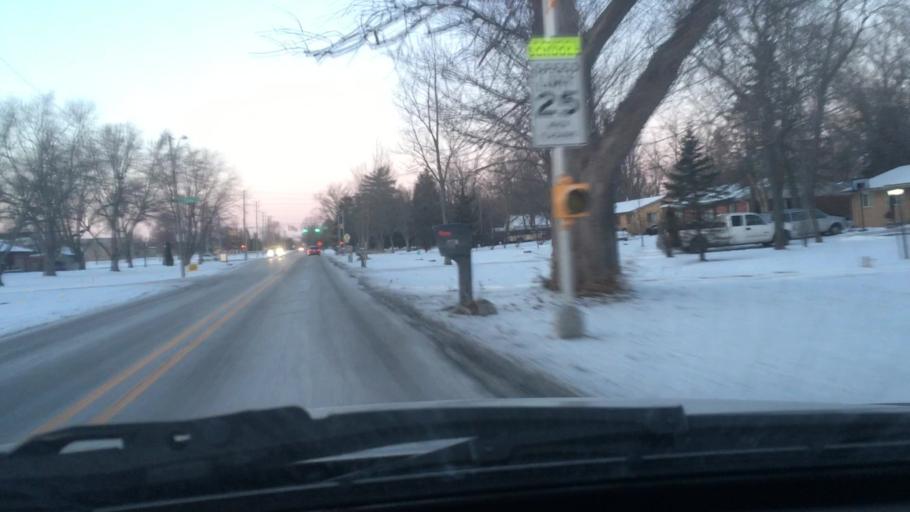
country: US
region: Indiana
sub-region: Marion County
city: Lawrence
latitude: 39.8817
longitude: -86.0330
